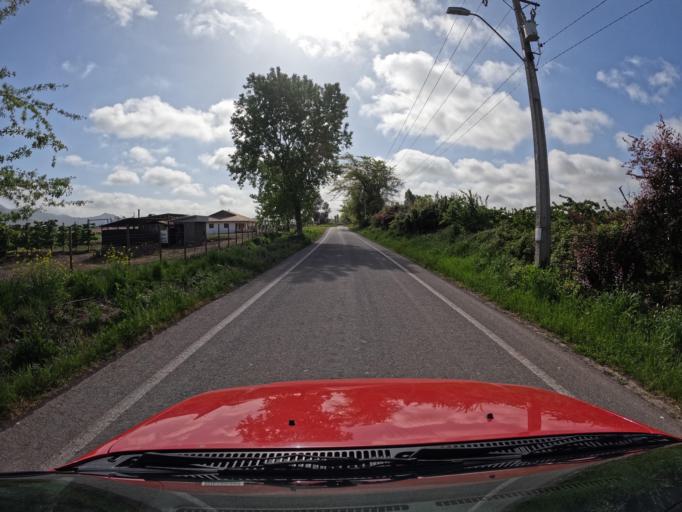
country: CL
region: Maule
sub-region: Provincia de Curico
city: Teno
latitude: -34.8802
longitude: -71.2370
